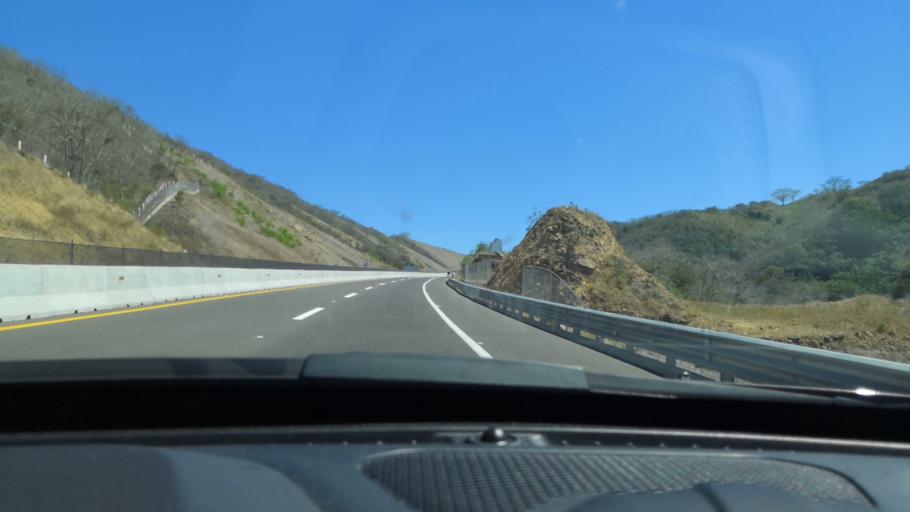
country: MX
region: Nayarit
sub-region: Compostela
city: Juan Escutia (Borbollon)
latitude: 21.1279
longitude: -104.8975
